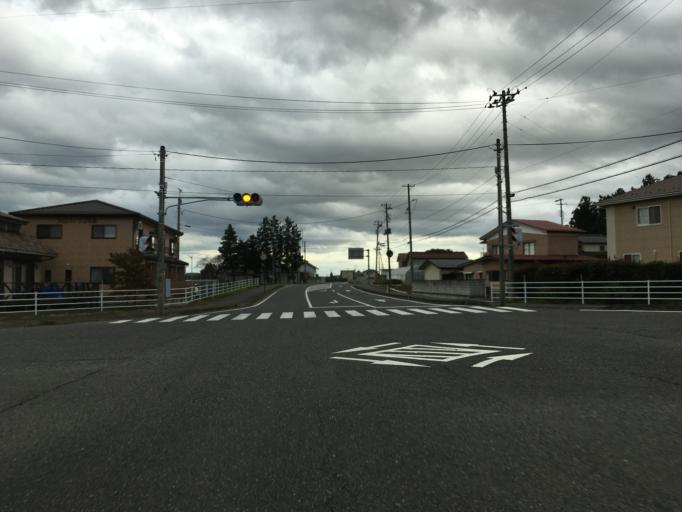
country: JP
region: Fukushima
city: Motomiya
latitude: 37.5455
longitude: 140.3842
